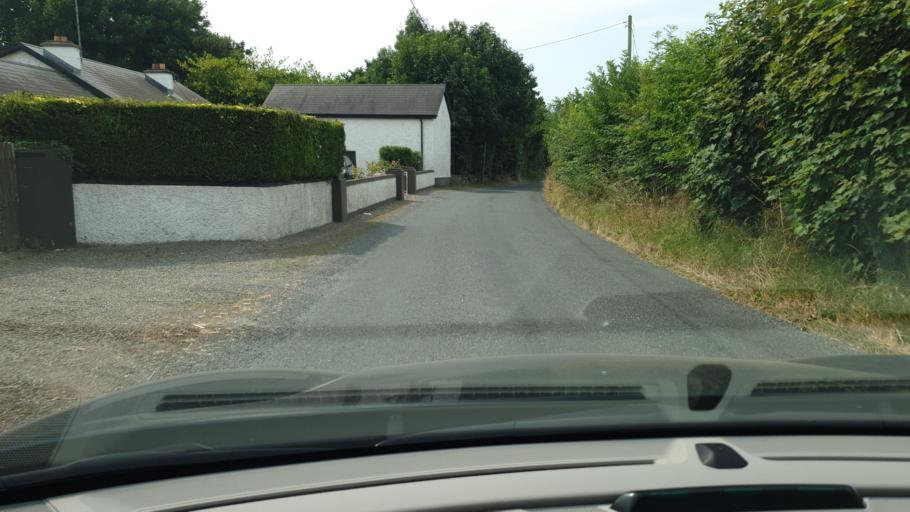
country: IE
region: Leinster
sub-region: An Mhi
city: Athboy
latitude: 53.6612
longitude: -6.9375
